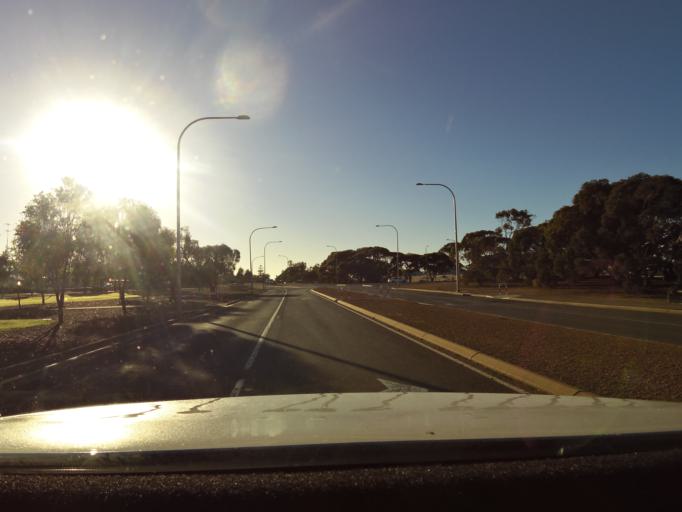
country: AU
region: South Australia
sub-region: Berri and Barmera
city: Berri
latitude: -34.2818
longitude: 140.5983
